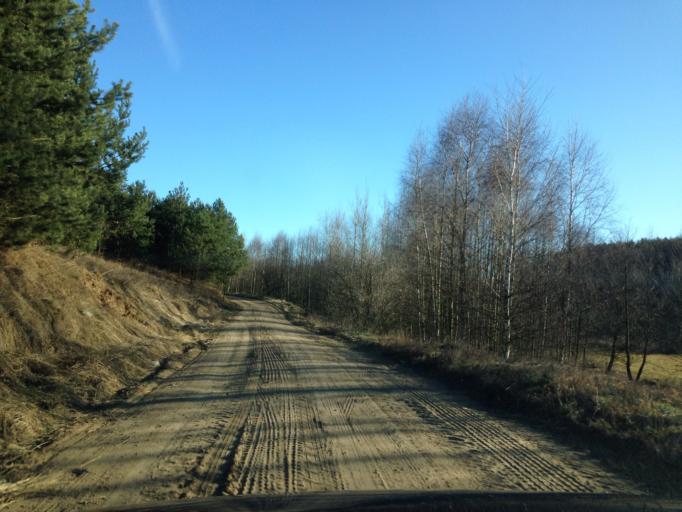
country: PL
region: Kujawsko-Pomorskie
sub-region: Powiat brodnicki
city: Brzozie
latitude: 53.3037
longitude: 19.6552
